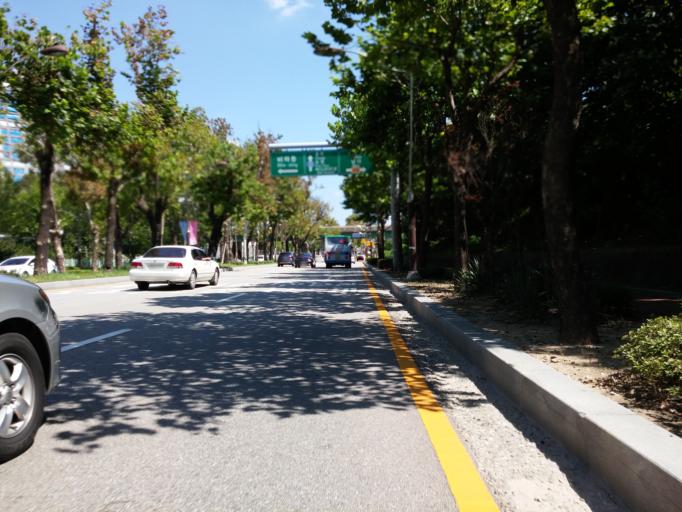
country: KR
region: Chungcheongbuk-do
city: Cheongju-si
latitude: 36.6262
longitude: 127.4188
